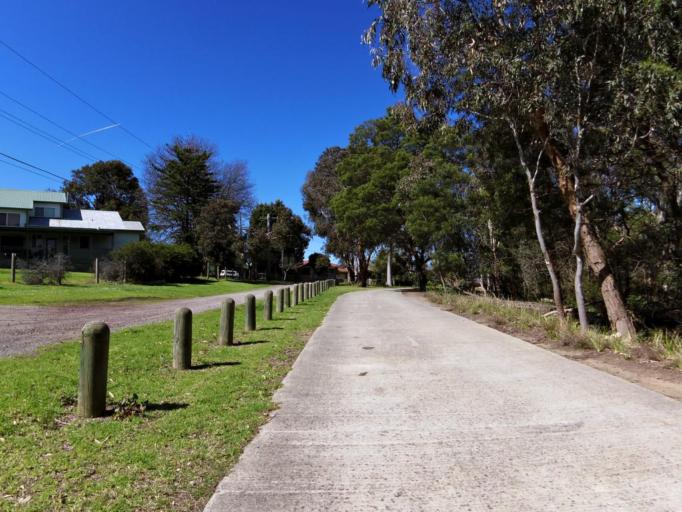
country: AU
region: Victoria
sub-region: Greater Dandenong
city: Dandenong
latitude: -37.9750
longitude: 145.1948
